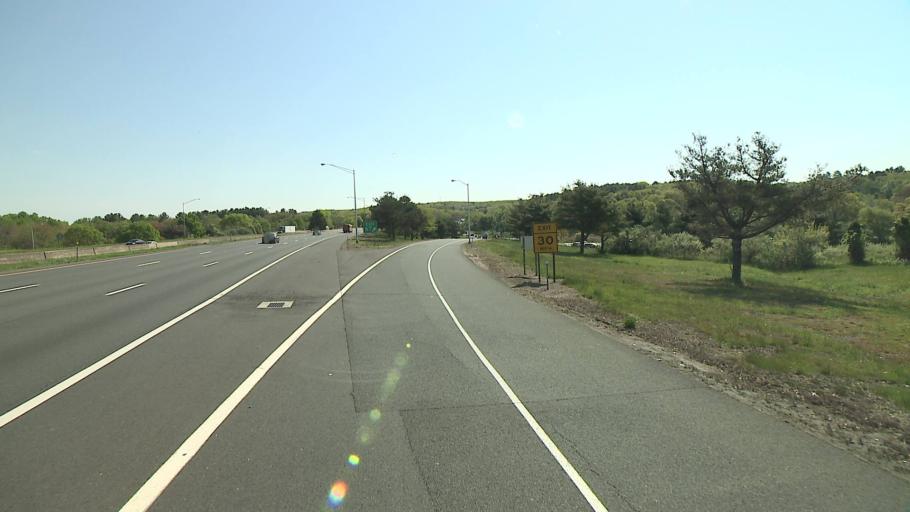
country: US
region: Connecticut
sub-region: Tolland County
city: Rockville
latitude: 41.8534
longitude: -72.4318
